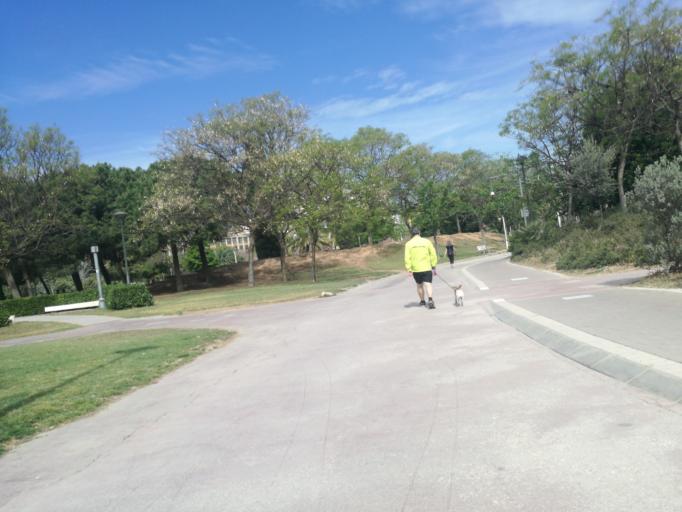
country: ES
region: Valencia
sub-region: Provincia de Valencia
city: Valencia
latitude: 39.4604
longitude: -0.3570
